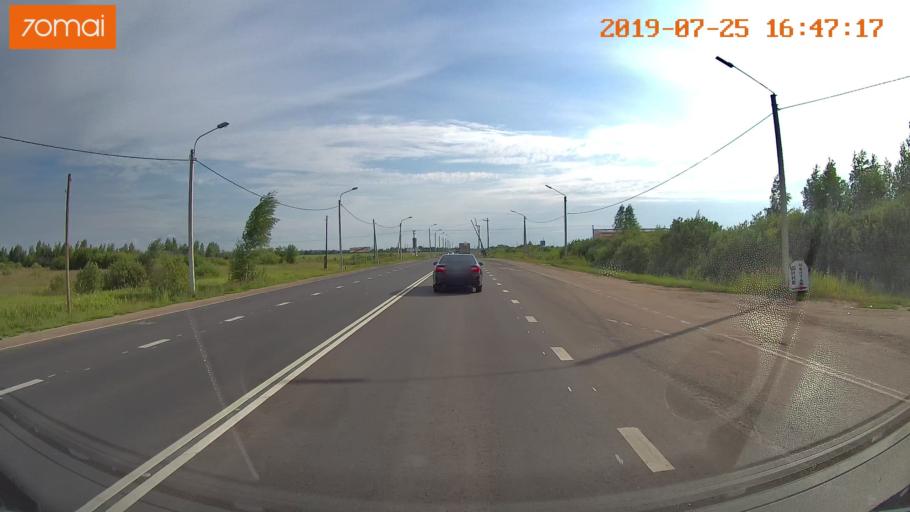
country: RU
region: Ivanovo
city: Privolzhsk
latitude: 57.3664
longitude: 41.2720
